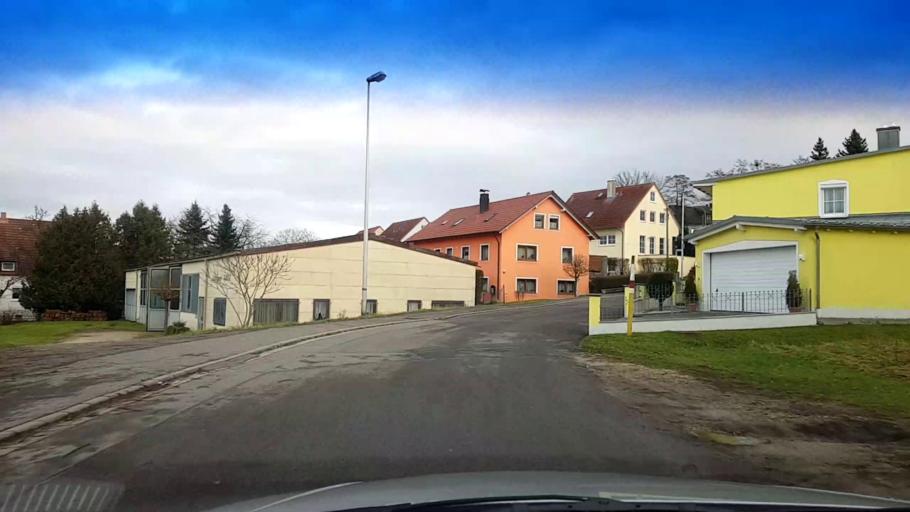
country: DE
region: Bavaria
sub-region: Upper Franconia
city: Litzendorf
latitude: 49.9089
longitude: 10.9989
